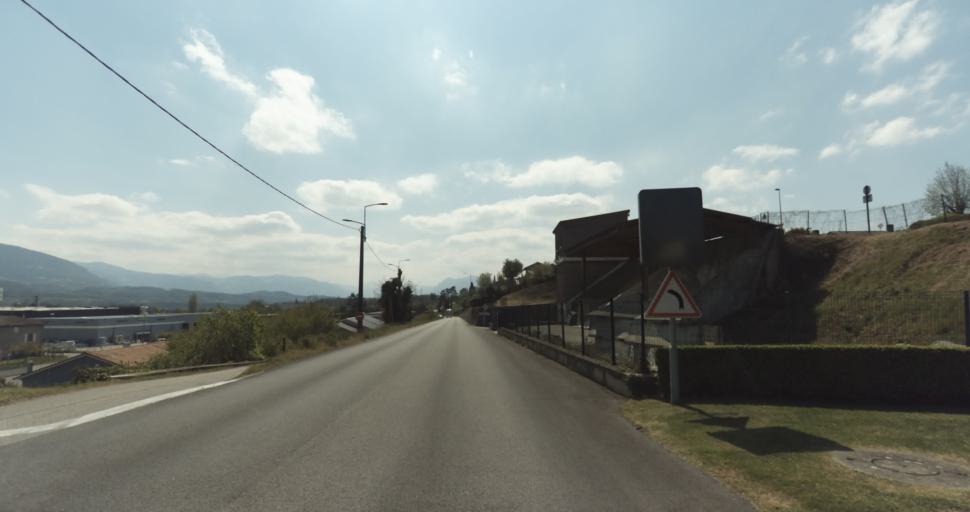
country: FR
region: Rhone-Alpes
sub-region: Departement de l'Isere
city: Saint-Marcellin
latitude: 45.1431
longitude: 5.3267
